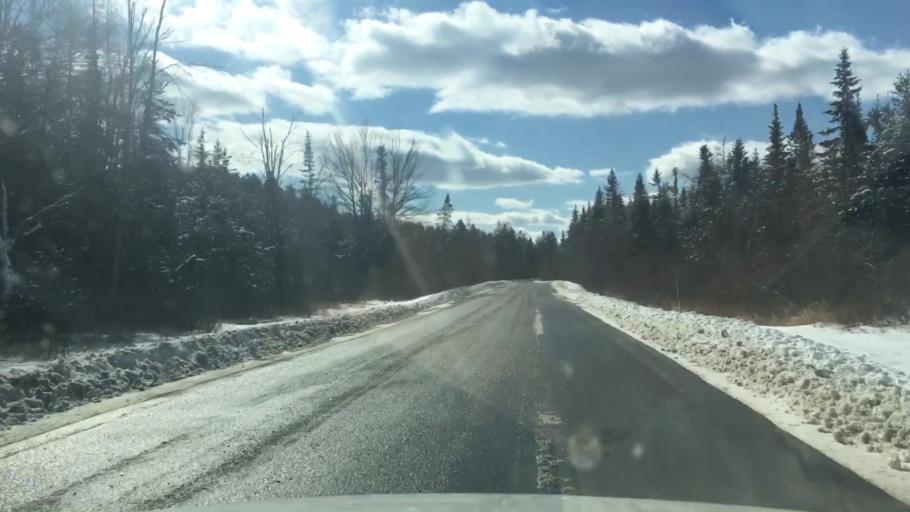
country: US
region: Maine
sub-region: Washington County
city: Machiasport
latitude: 44.6769
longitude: -67.4173
